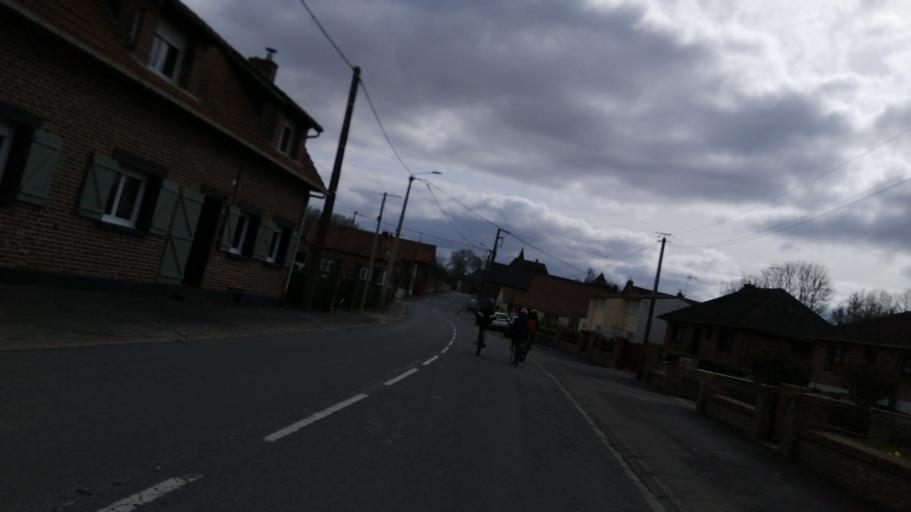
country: FR
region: Nord-Pas-de-Calais
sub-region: Departement du Pas-de-Calais
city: Beaurains
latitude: 50.2153
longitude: 2.8197
